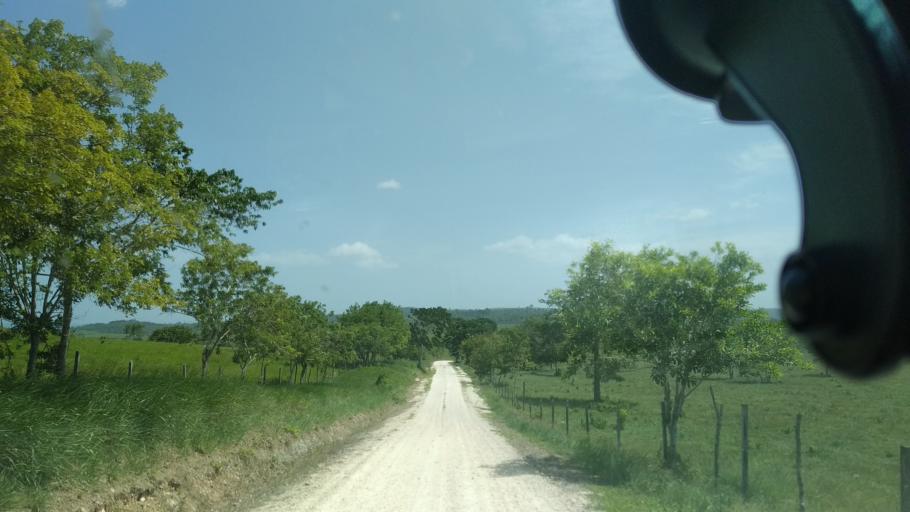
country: BZ
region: Cayo
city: San Ignacio
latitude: 17.2937
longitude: -89.0644
